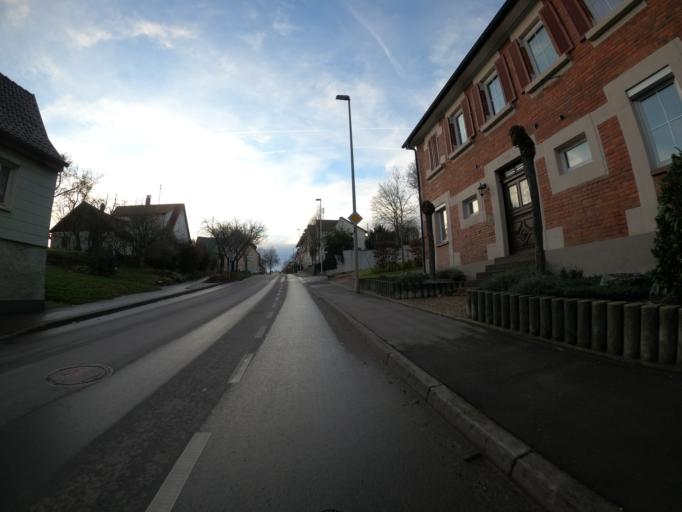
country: DE
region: Baden-Wuerttemberg
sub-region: Regierungsbezirk Stuttgart
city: Hattenhofen
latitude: 48.6671
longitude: 9.5697
